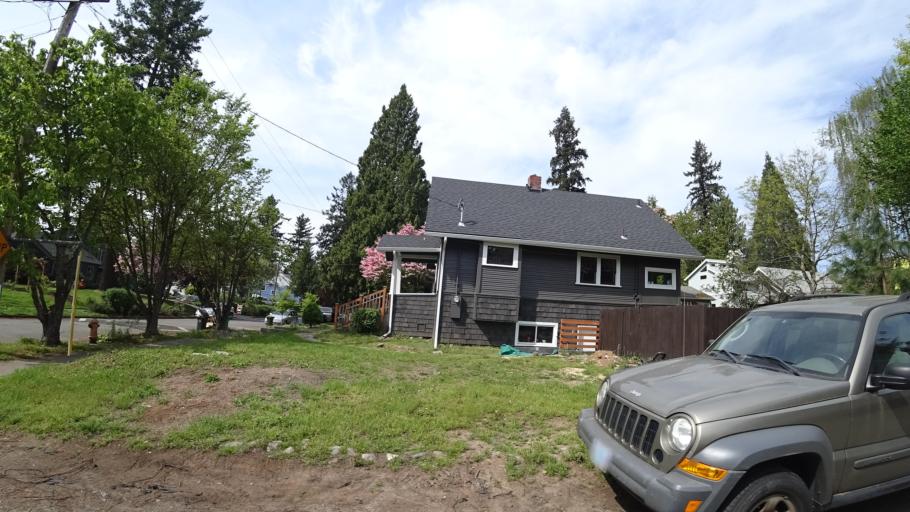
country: US
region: Oregon
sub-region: Clackamas County
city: Milwaukie
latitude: 45.4828
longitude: -122.6173
